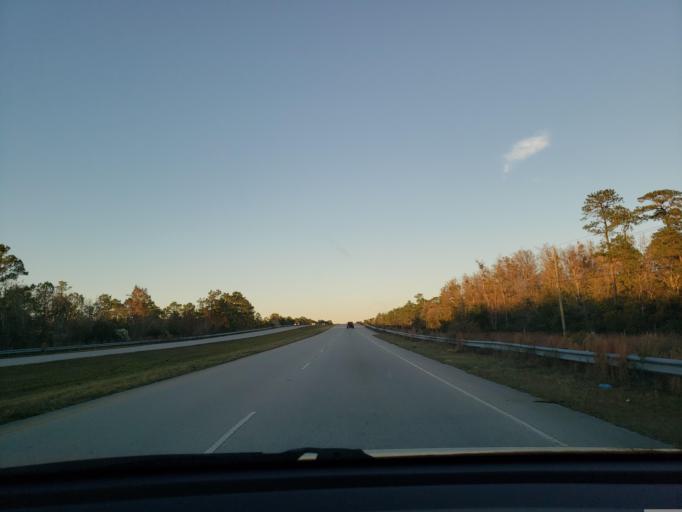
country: US
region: North Carolina
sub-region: Onslow County
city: Sneads Ferry
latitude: 34.6320
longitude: -77.4808
